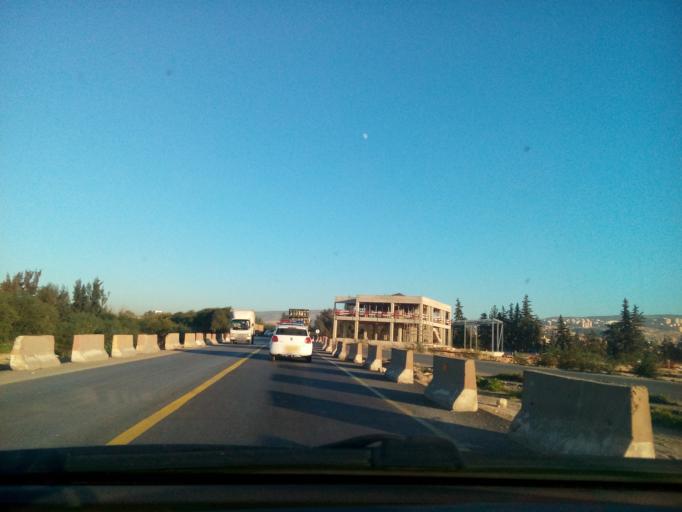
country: DZ
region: Relizane
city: Oued Rhiou
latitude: 35.9679
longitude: 0.9056
